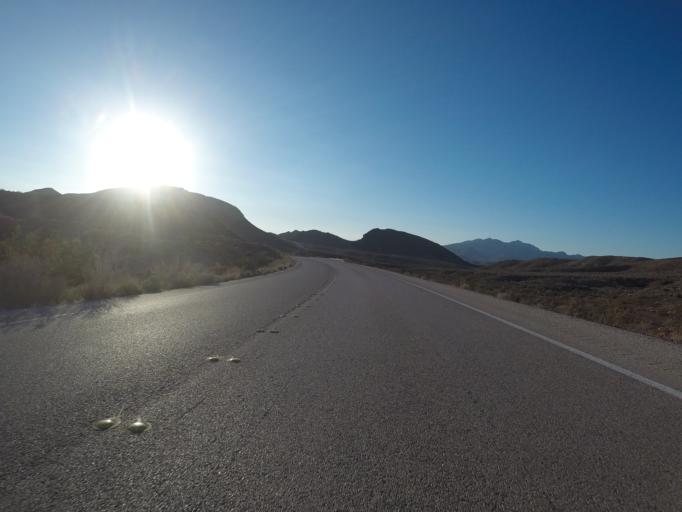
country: US
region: Nevada
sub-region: Clark County
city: Moapa Valley
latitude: 36.2434
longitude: -114.5367
